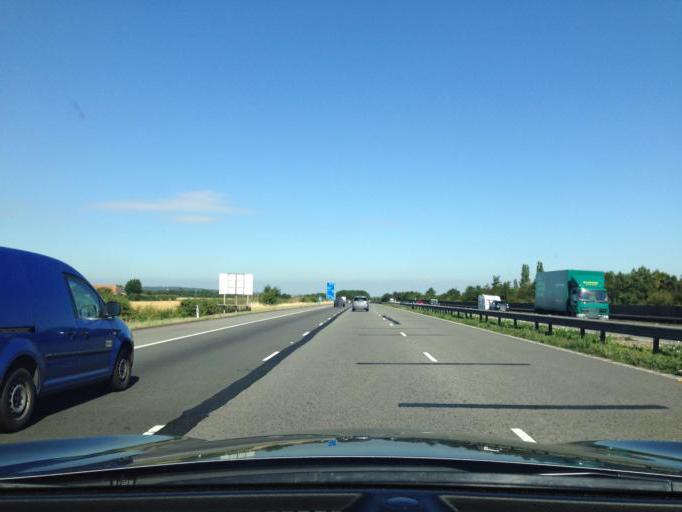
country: GB
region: England
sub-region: Oxfordshire
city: Chalgrove
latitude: 51.7292
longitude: -1.0684
